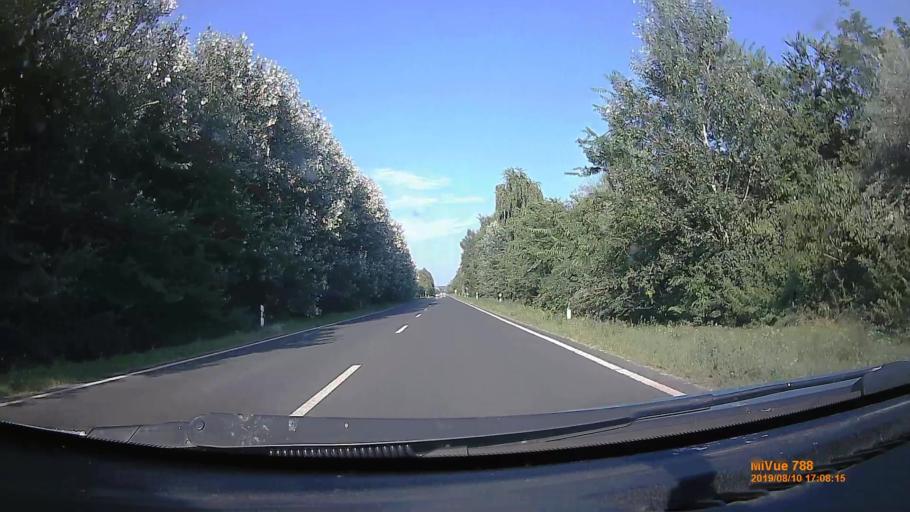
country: HU
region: Somogy
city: Fonyod
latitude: 46.7624
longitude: 17.6037
